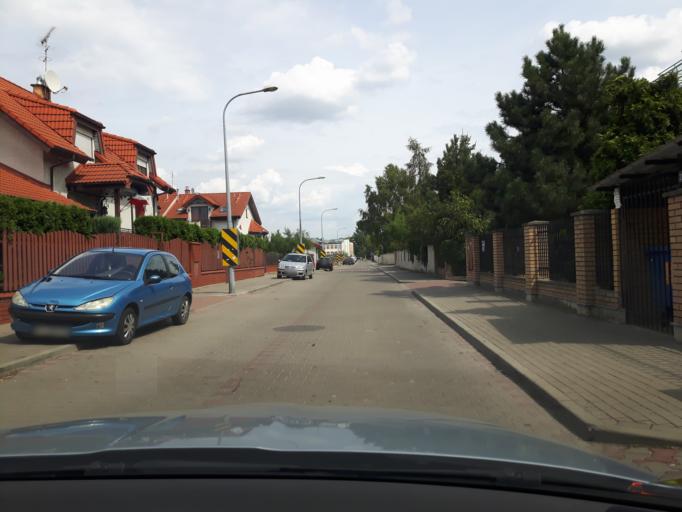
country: PL
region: Masovian Voivodeship
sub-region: Warszawa
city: Ursynow
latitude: 52.1461
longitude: 21.0112
